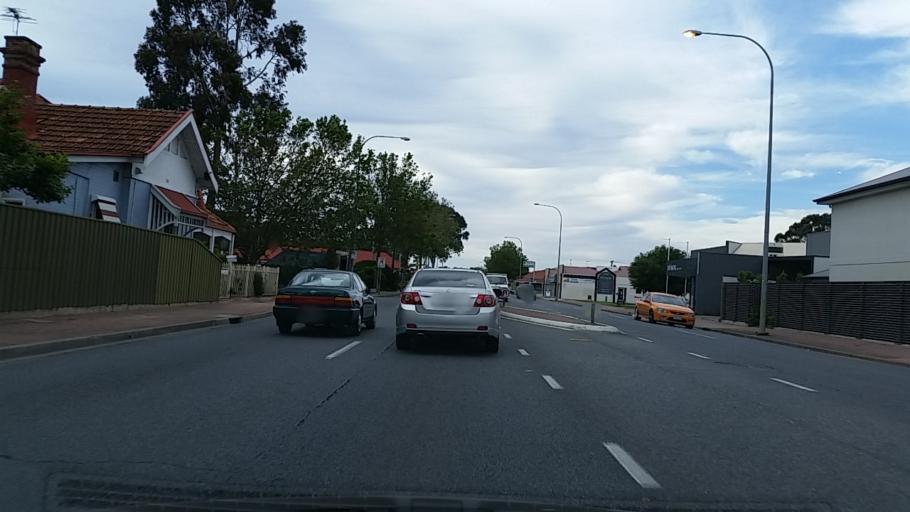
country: AU
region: South Australia
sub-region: City of West Torrens
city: Thebarton
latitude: -34.9180
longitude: 138.5677
